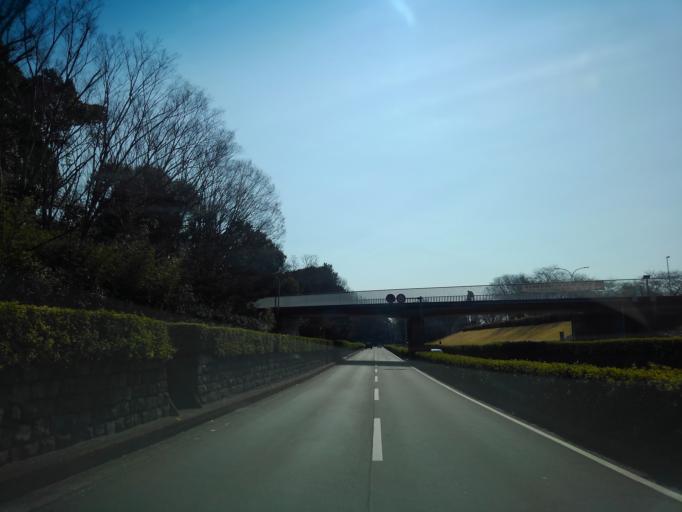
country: JP
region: Saitama
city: Tokorozawa
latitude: 35.7980
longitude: 139.4686
